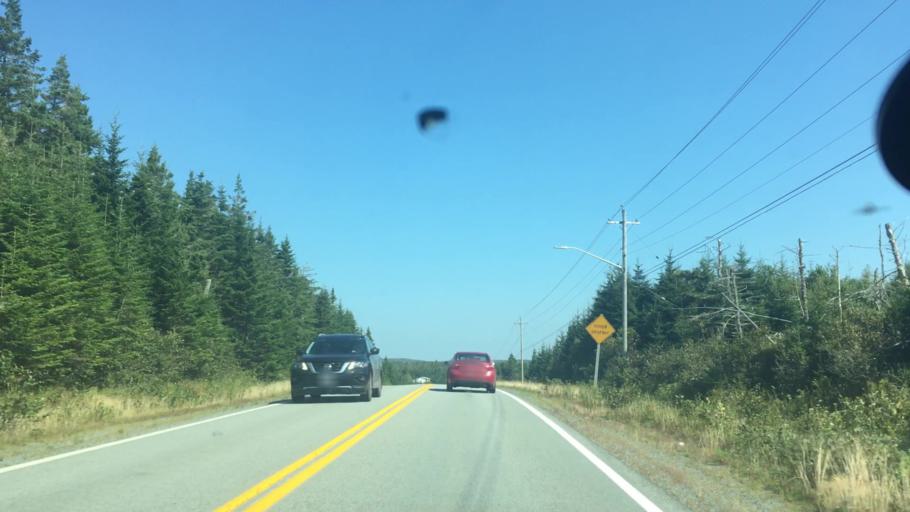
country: CA
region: Nova Scotia
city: Antigonish
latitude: 44.9388
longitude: -62.2684
